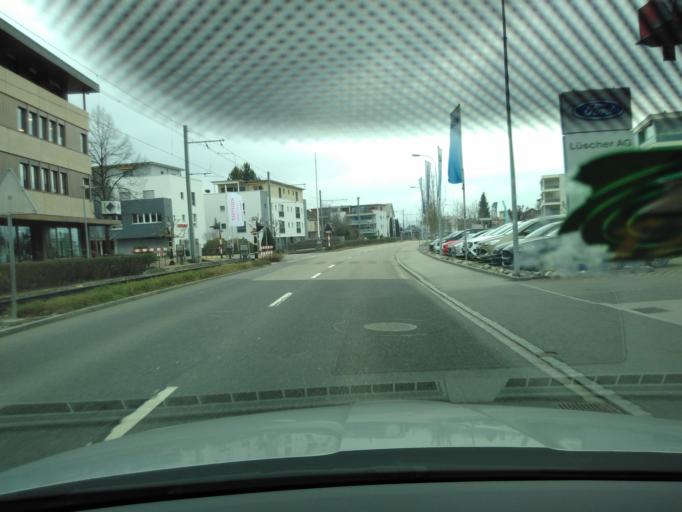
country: CH
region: Aargau
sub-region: Bezirk Aarau
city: Muhen
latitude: 47.3362
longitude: 8.0541
